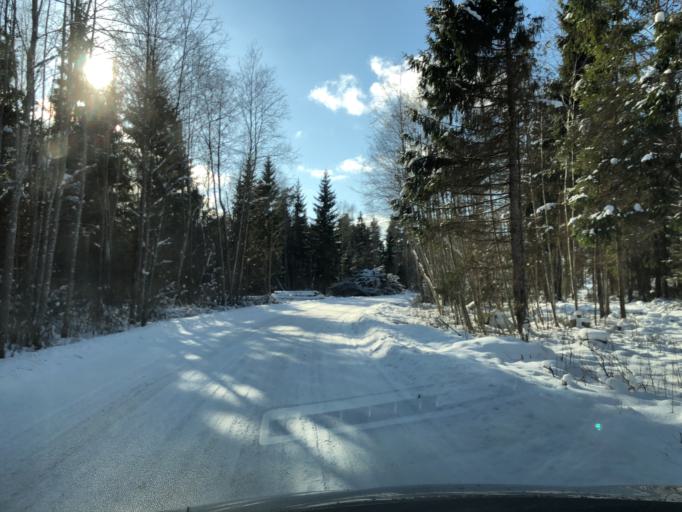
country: EE
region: Jaervamaa
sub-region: Paide linn
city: Paide
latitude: 59.0457
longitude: 25.4774
